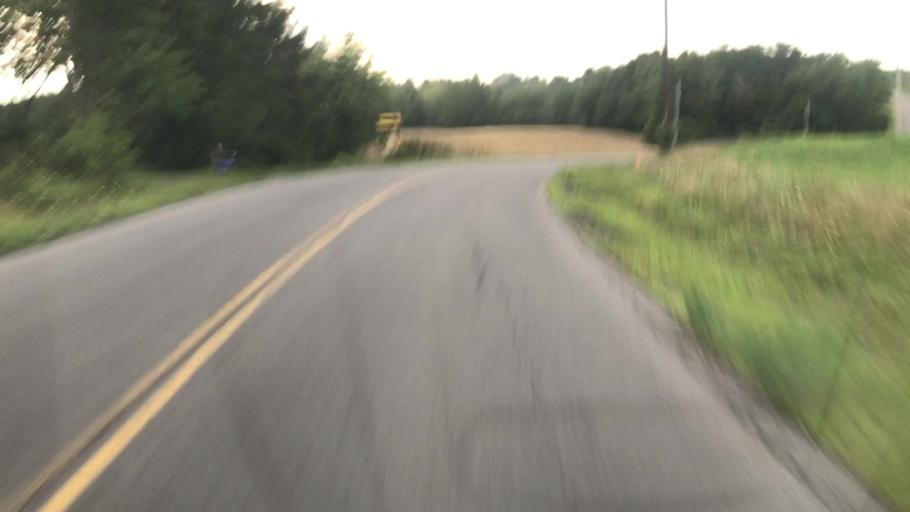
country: US
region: New York
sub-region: Cayuga County
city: Melrose Park
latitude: 42.9170
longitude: -76.5192
